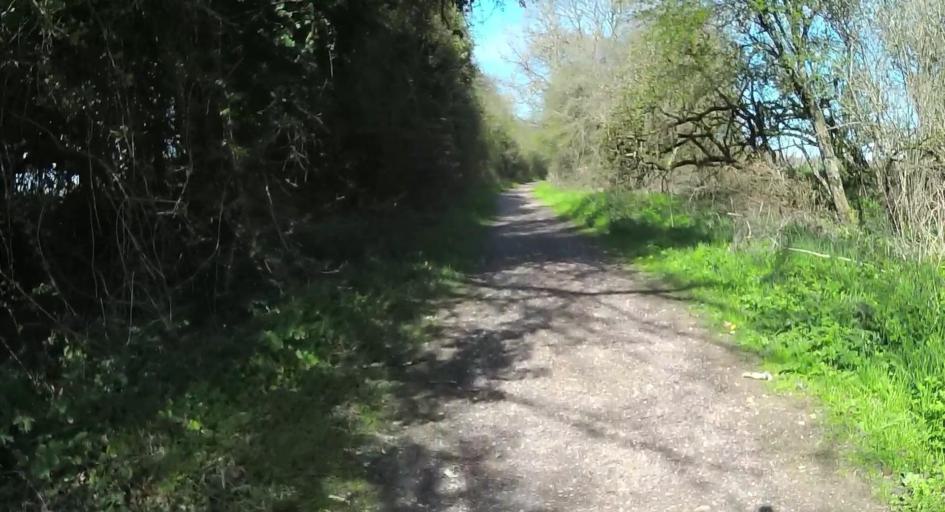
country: GB
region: England
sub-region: Hampshire
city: Romsey
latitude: 51.0687
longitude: -1.5139
